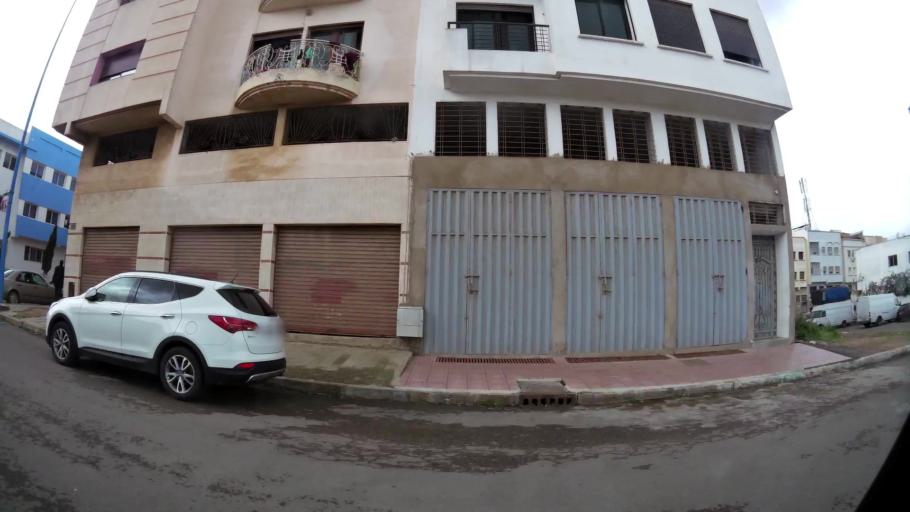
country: MA
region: Grand Casablanca
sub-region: Casablanca
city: Casablanca
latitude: 33.5669
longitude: -7.6924
